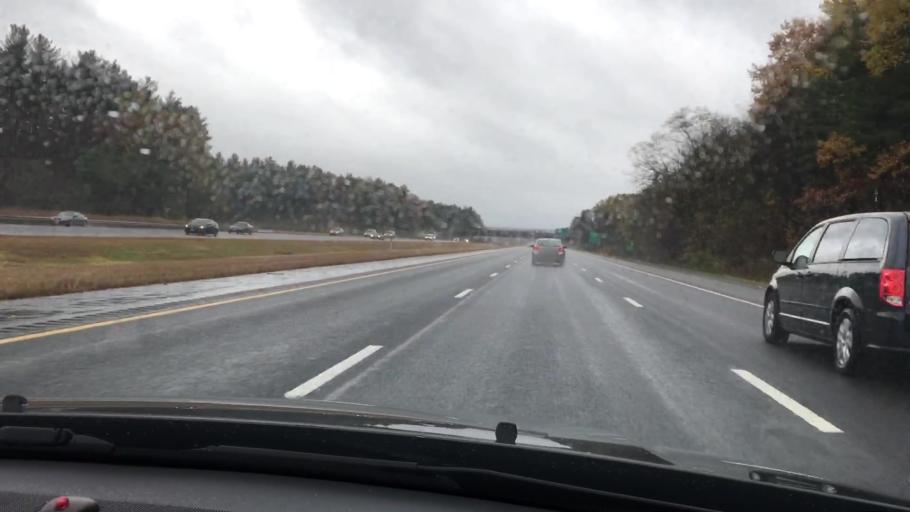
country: US
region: Massachusetts
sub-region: Middlesex County
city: Tyngsboro
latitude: 42.6845
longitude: -71.4425
